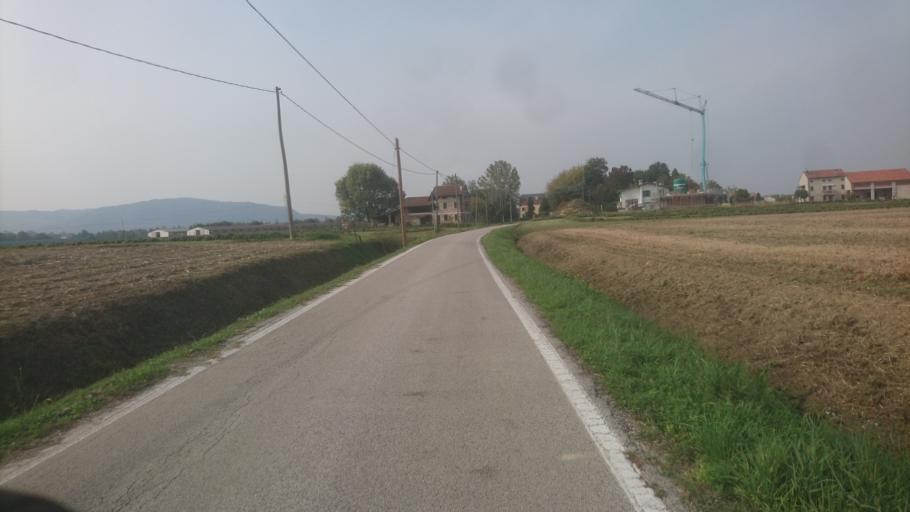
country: IT
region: Veneto
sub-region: Provincia di Vicenza
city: Montegalda
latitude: 45.4663
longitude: 11.6523
